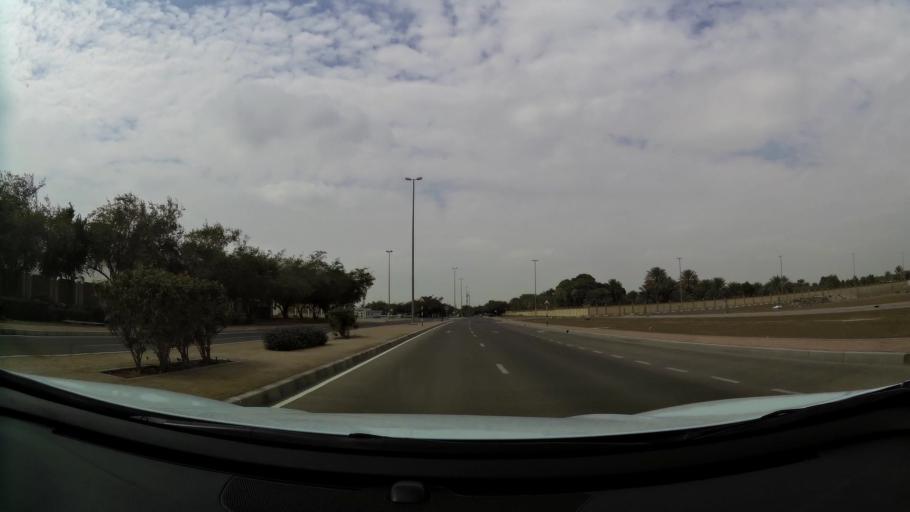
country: OM
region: Al Buraimi
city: Al Buraymi
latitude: 24.2134
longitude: 55.7922
